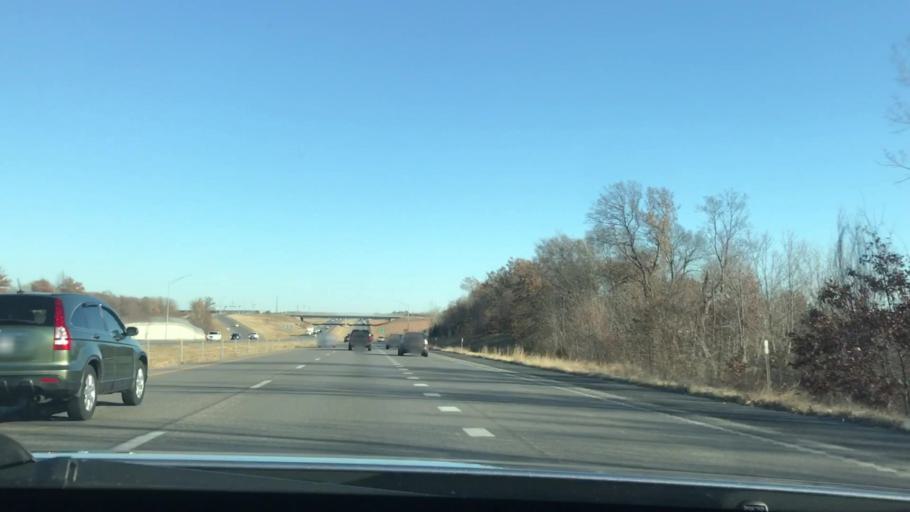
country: US
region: Missouri
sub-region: Platte County
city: Weatherby Lake
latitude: 39.2542
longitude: -94.6392
